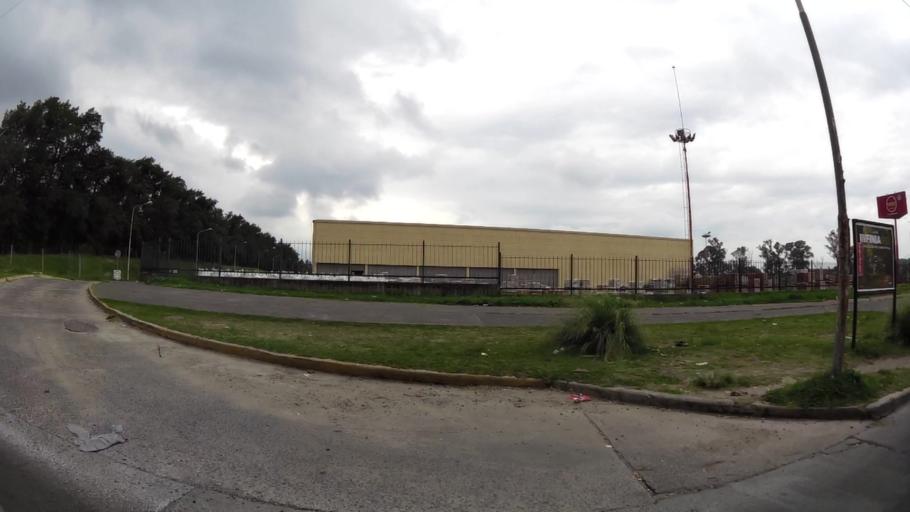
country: AR
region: Buenos Aires
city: San Justo
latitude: -34.6985
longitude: -58.5393
